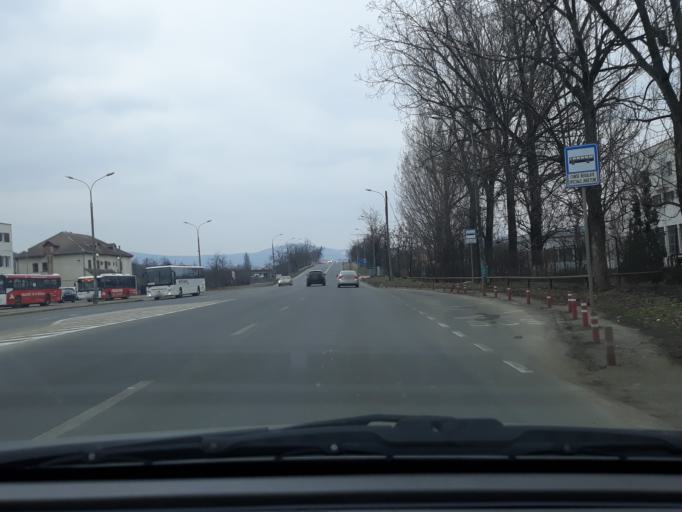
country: RO
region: Salaj
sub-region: Comuna Criseni
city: Criseni
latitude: 47.2211
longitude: 23.0401
